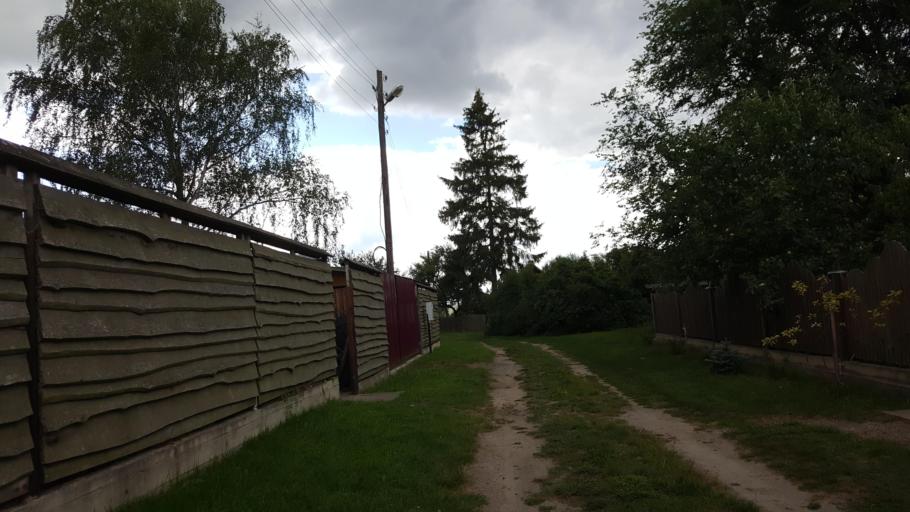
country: BY
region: Brest
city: Zhabinka
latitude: 52.2607
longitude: 23.9701
